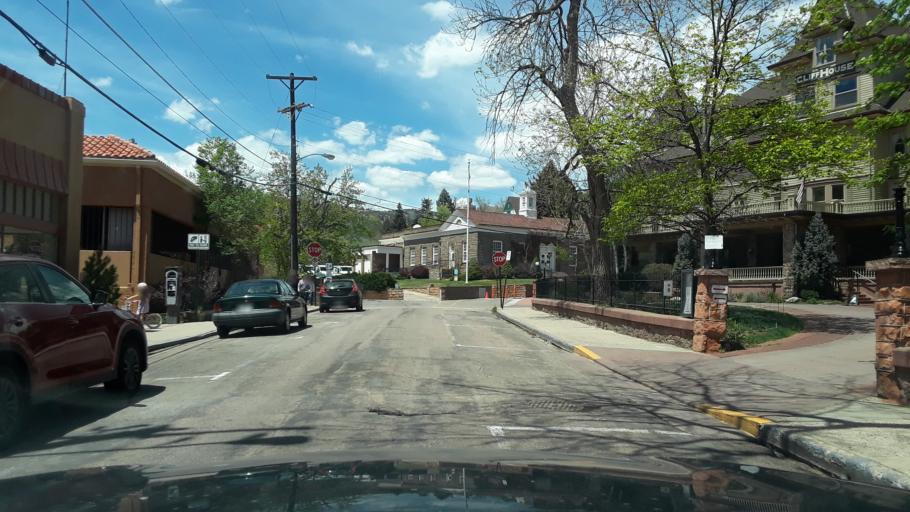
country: US
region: Colorado
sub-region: El Paso County
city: Manitou Springs
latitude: 38.8593
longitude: -104.9174
